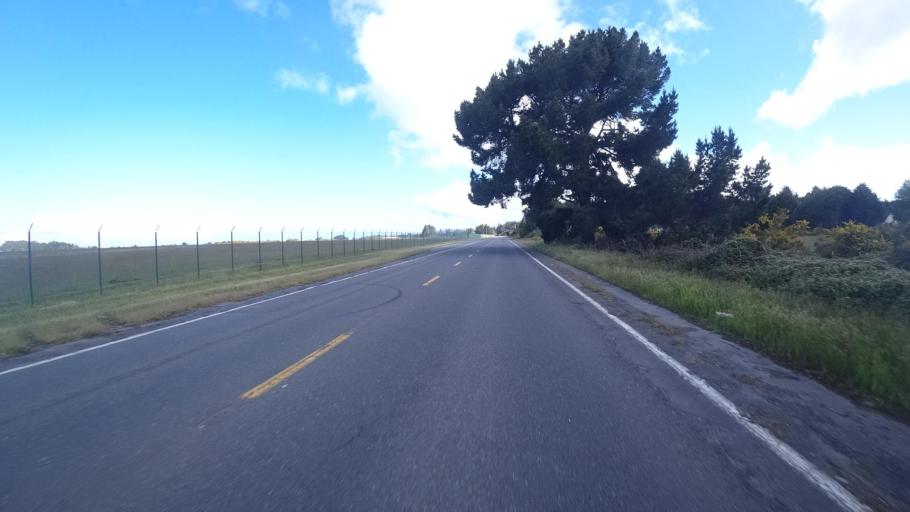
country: US
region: California
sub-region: Humboldt County
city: McKinleyville
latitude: 40.9723
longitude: -124.1006
